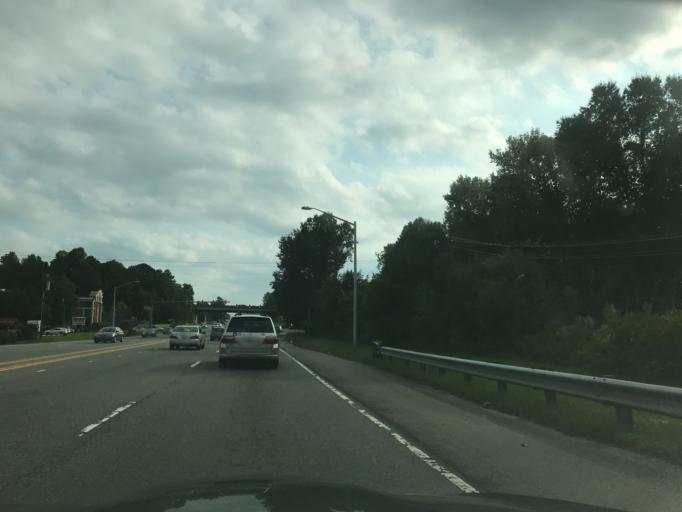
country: US
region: North Carolina
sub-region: Durham County
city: Durham
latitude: 35.9097
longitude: -78.8934
